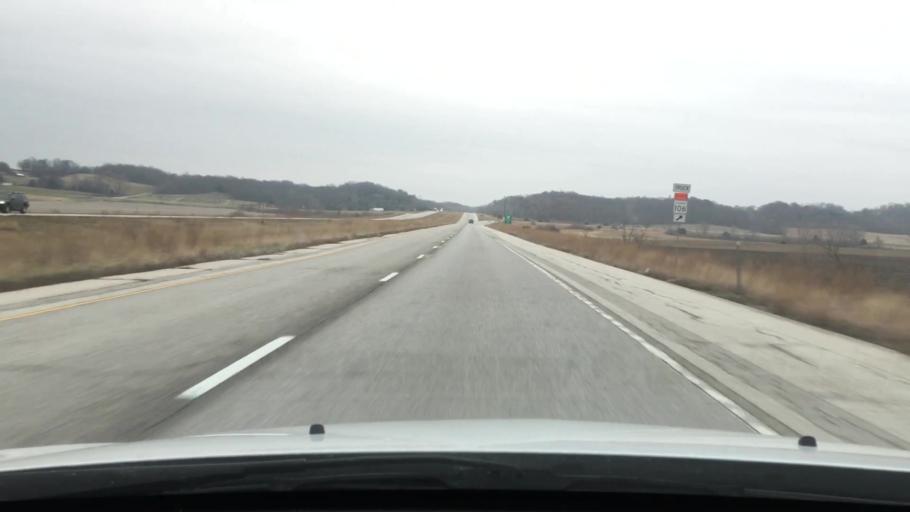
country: US
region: Illinois
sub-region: Scott County
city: Winchester
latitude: 39.6850
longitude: -90.5828
